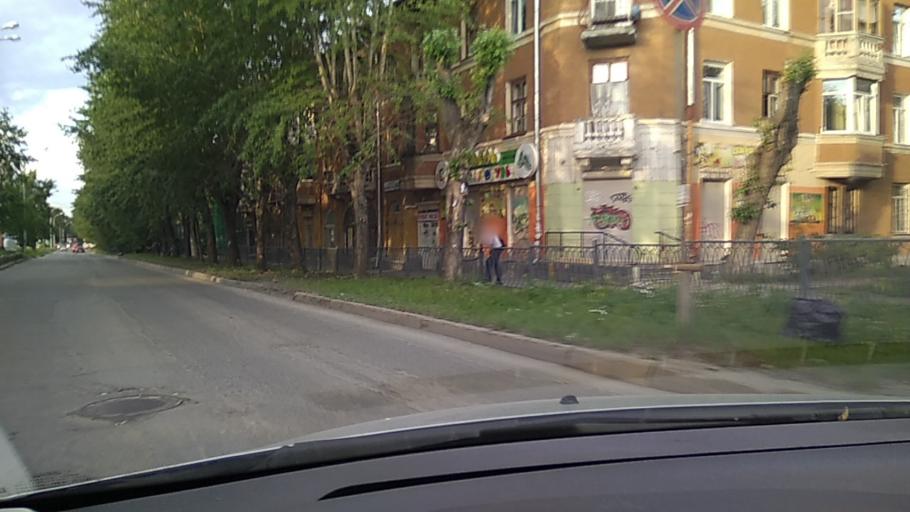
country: RU
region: Sverdlovsk
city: Yekaterinburg
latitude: 56.9000
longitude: 60.5886
